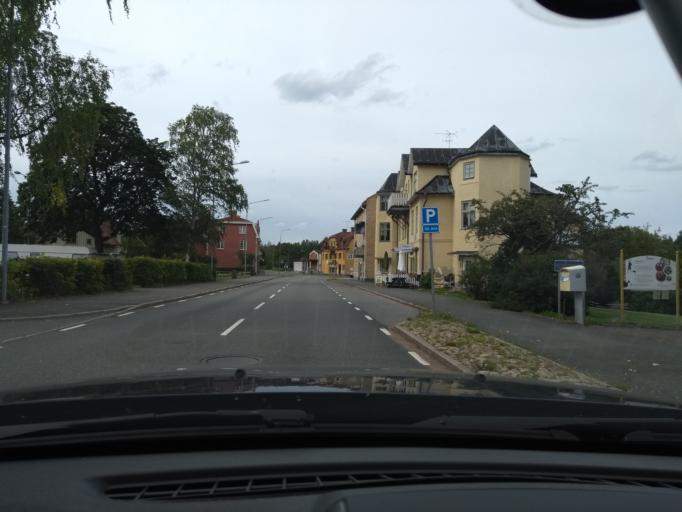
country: SE
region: Joenkoeping
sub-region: Eksjo Kommun
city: Mariannelund
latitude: 57.6156
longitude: 15.5741
